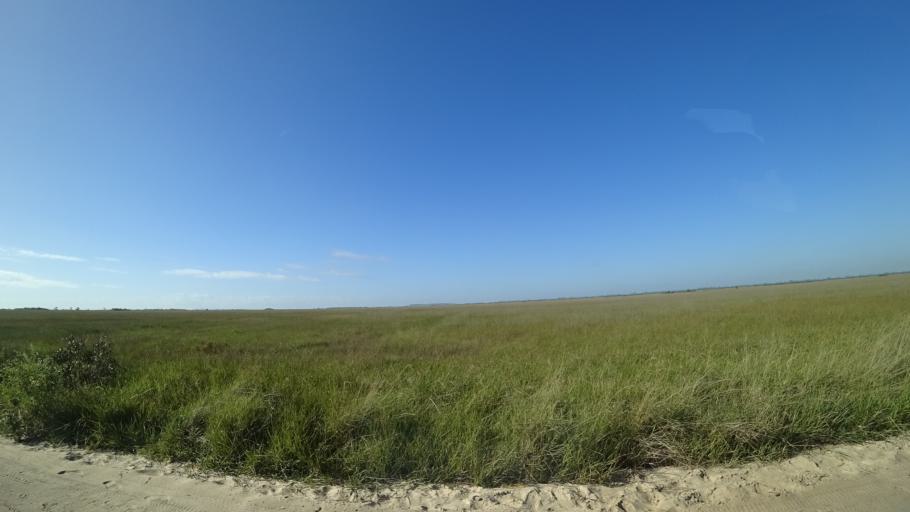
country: MZ
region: Sofala
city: Beira
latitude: -19.7523
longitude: 34.9333
